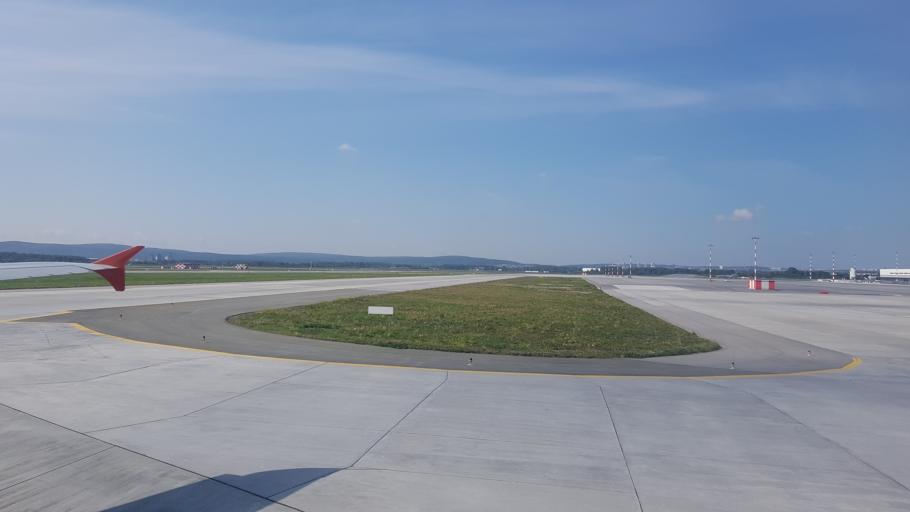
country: RU
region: Sverdlovsk
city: Istok
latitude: 56.7468
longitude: 60.8013
